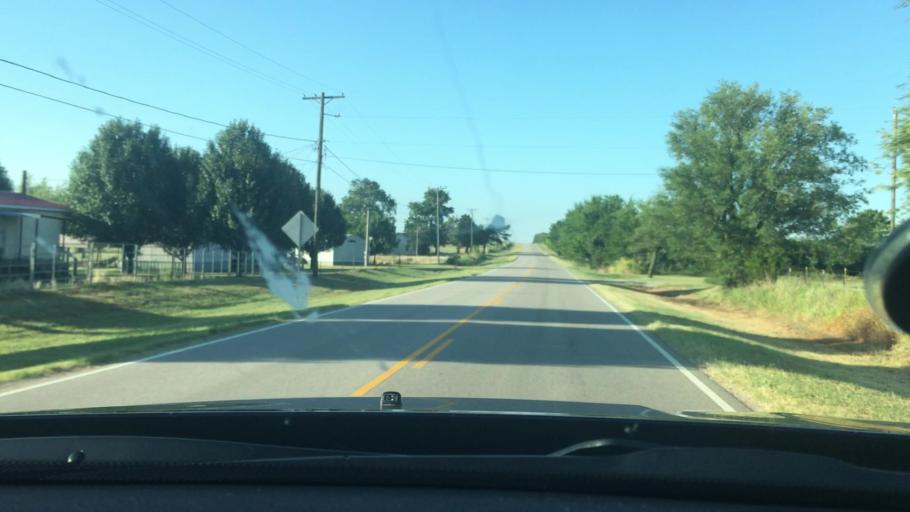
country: US
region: Oklahoma
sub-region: Murray County
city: Sulphur
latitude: 34.6149
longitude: -96.8448
